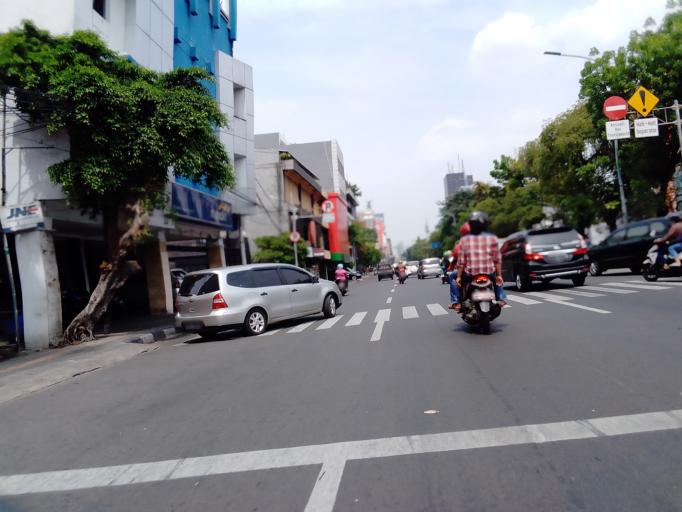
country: ID
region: Jakarta Raya
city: Jakarta
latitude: -6.1543
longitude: 106.8181
